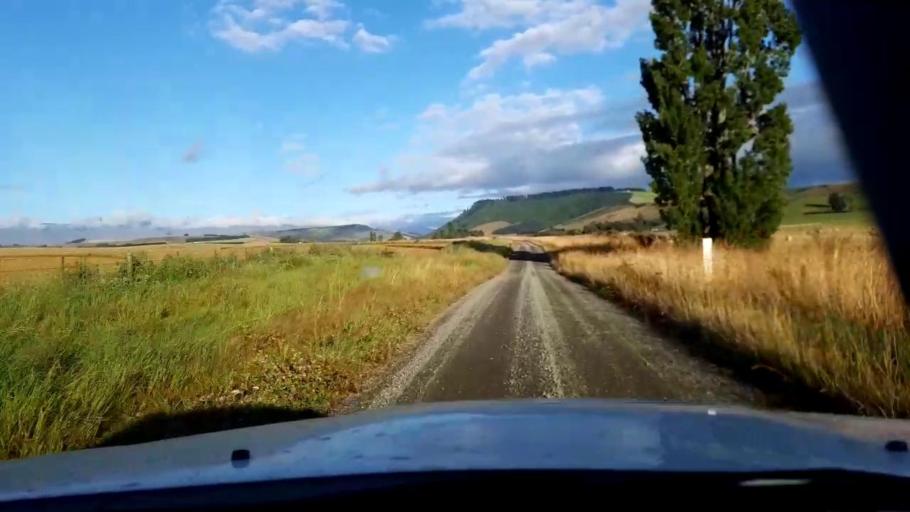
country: NZ
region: Canterbury
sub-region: Timaru District
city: Timaru
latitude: -44.4277
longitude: 171.1198
